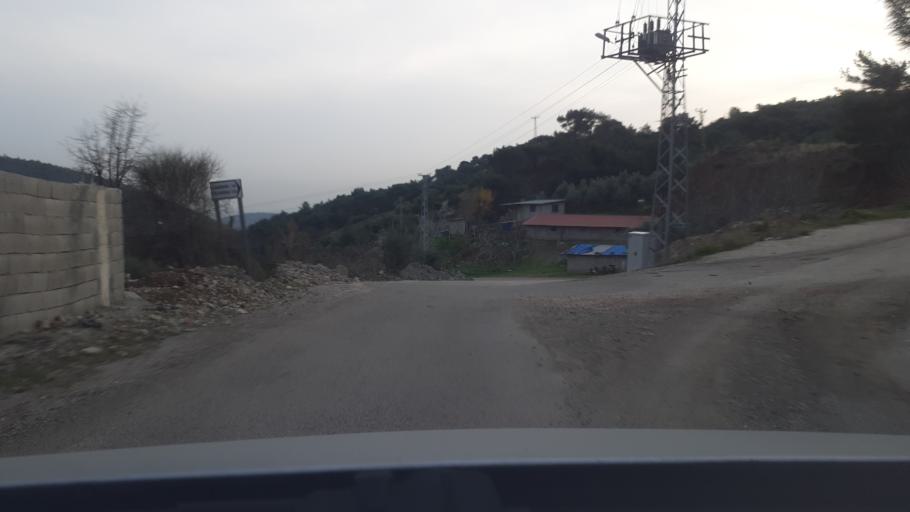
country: TR
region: Hatay
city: Kirikhan
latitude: 36.5284
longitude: 36.3167
